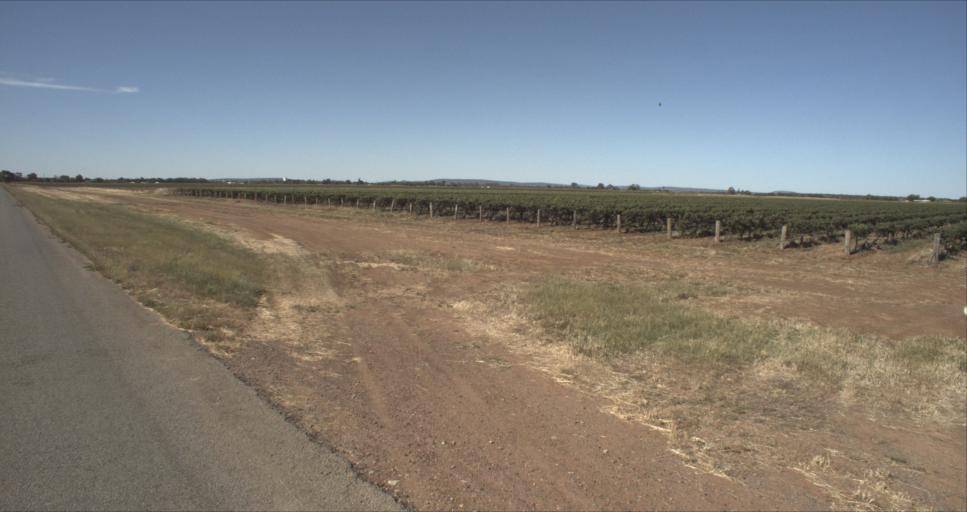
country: AU
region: New South Wales
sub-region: Leeton
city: Leeton
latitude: -34.5845
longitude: 146.3792
